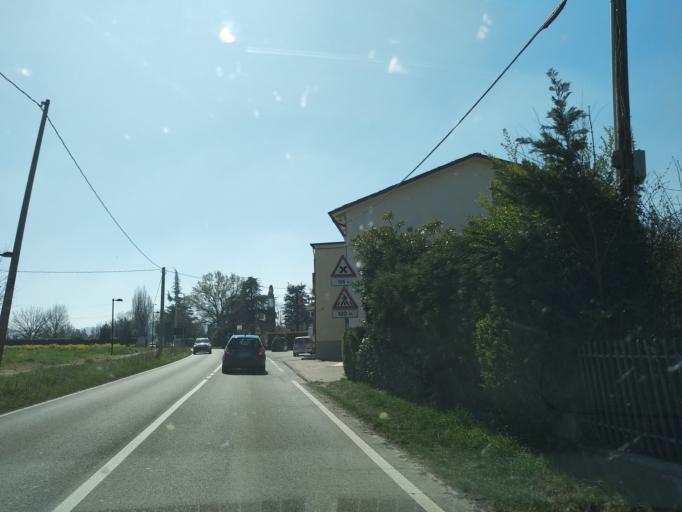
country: IT
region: Emilia-Romagna
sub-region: Provincia di Reggio Emilia
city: Albinea
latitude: 44.6469
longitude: 10.6079
